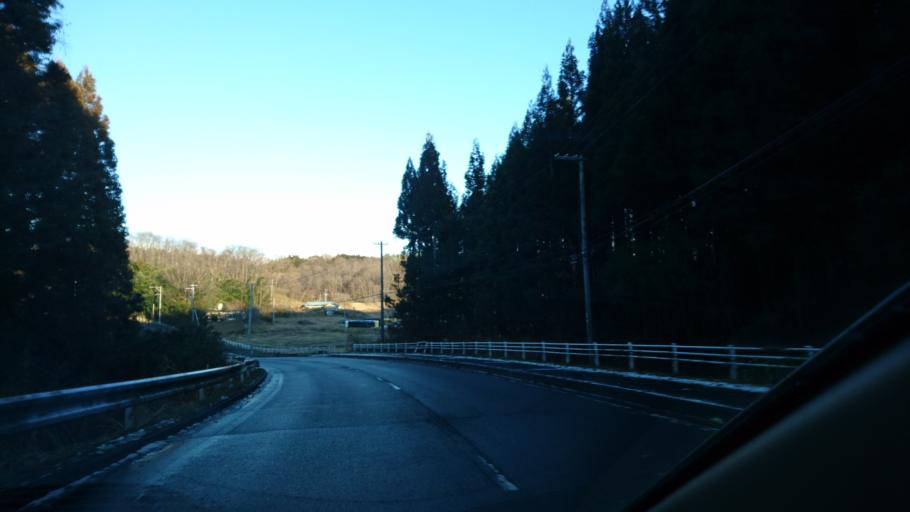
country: JP
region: Miyagi
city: Furukawa
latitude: 38.6602
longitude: 140.9016
